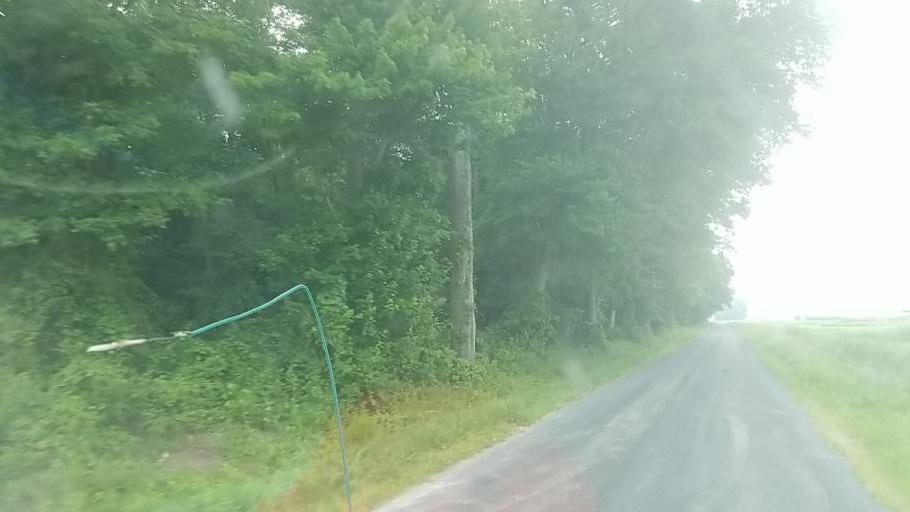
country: US
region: Delaware
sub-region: Sussex County
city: Selbyville
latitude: 38.4446
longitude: -75.2711
